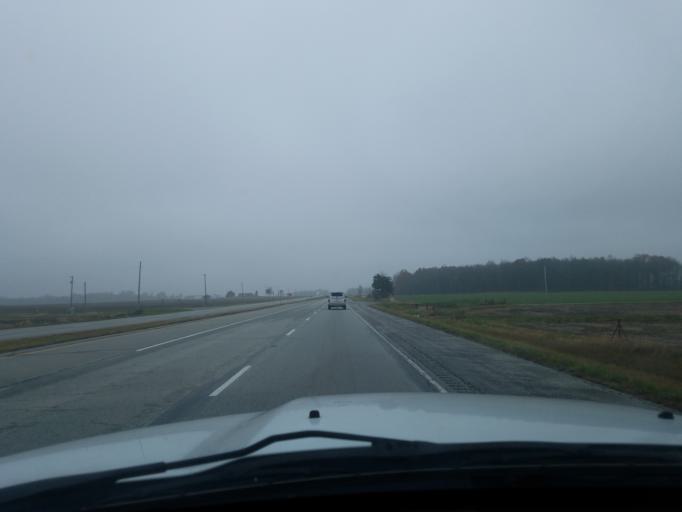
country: US
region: Indiana
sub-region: Tipton County
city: Tipton
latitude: 40.2379
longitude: -86.1277
